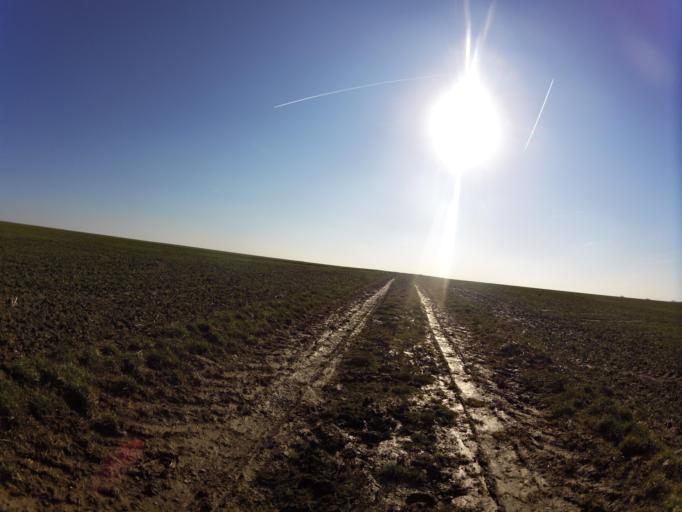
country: DE
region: Bavaria
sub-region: Regierungsbezirk Unterfranken
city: Giebelstadt
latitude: 49.6866
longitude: 9.9702
